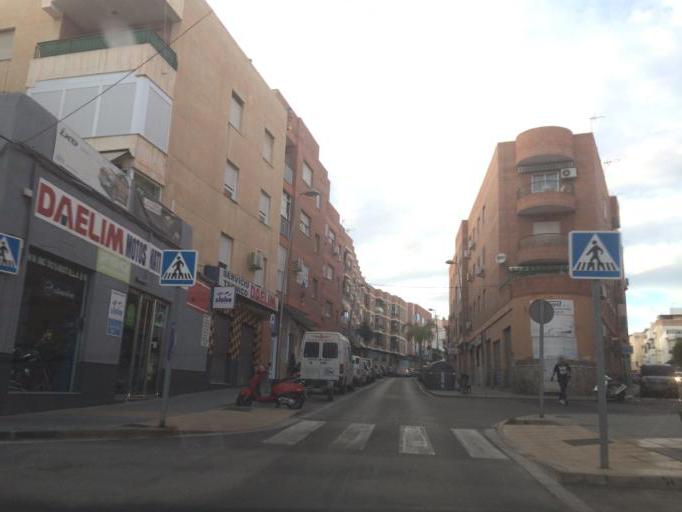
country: ES
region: Andalusia
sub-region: Provincia de Almeria
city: Almeria
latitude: 36.8473
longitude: -2.4682
